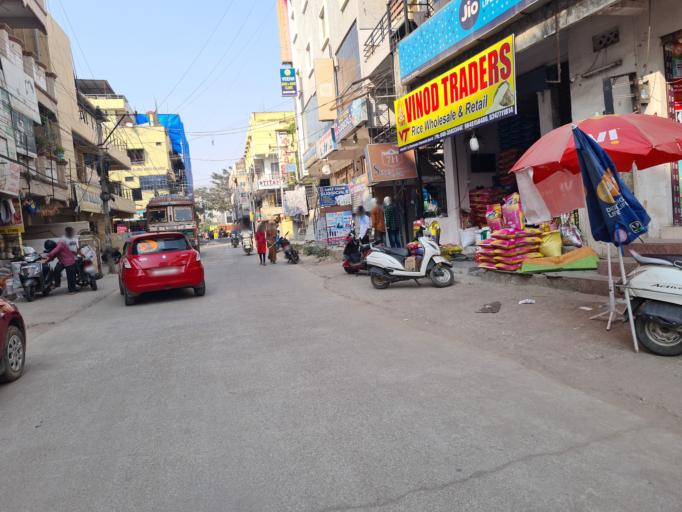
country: IN
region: Telangana
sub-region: Medak
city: Serilingampalle
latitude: 17.4939
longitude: 78.3181
